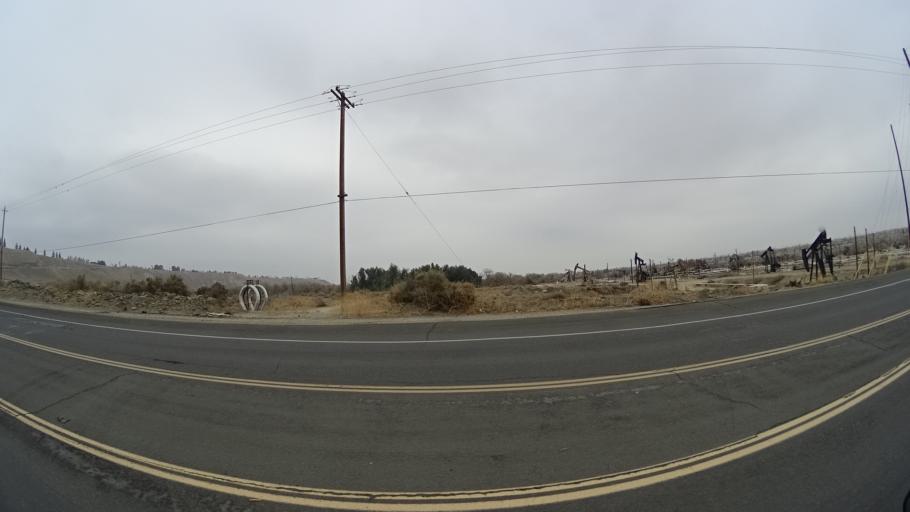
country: US
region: California
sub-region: Kern County
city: Oildale
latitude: 35.4209
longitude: -118.9671
